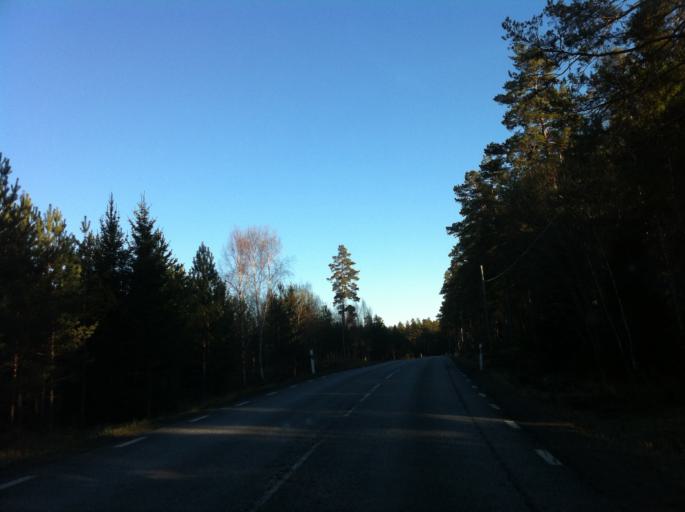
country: SE
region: Uppsala
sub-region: Osthammars Kommun
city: Anneberg
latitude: 60.1721
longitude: 18.4057
